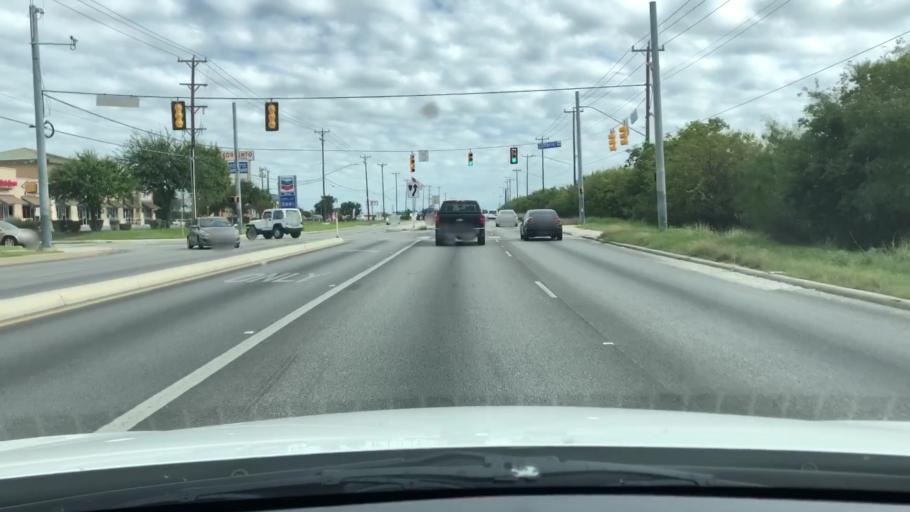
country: US
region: Texas
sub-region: Bexar County
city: Leon Valley
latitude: 29.4905
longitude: -98.6823
